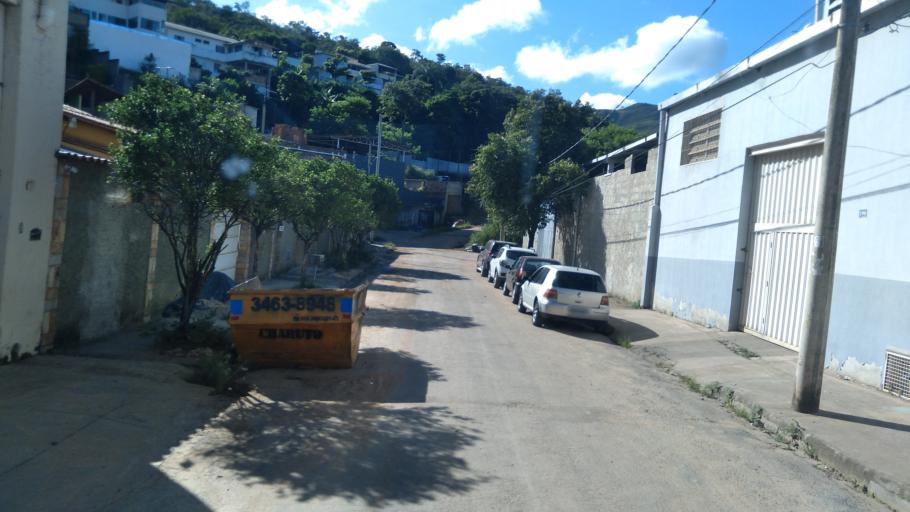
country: BR
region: Minas Gerais
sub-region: Belo Horizonte
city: Belo Horizonte
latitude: -19.9207
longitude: -43.8979
